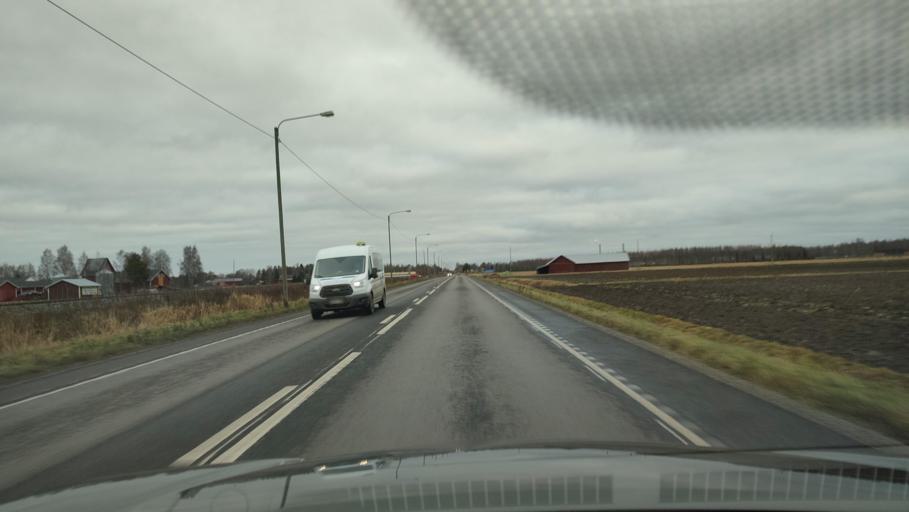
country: FI
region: Southern Ostrobothnia
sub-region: Seinaejoki
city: Ilmajoki
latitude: 62.7202
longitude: 22.5643
